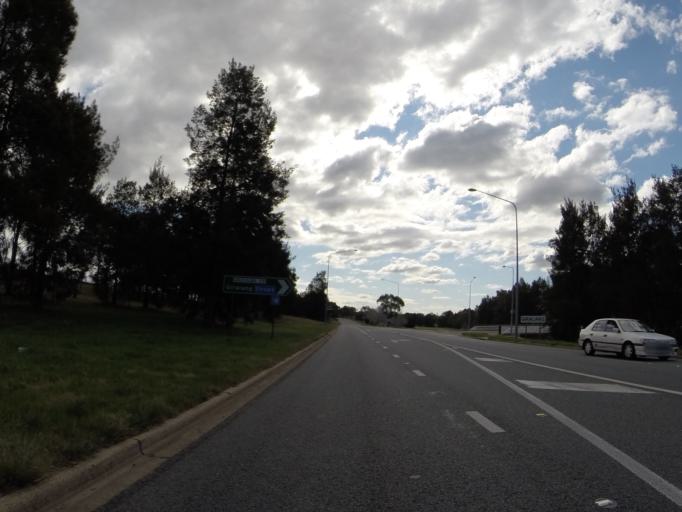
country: AU
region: Australian Capital Territory
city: Kaleen
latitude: -35.2195
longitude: 149.0980
